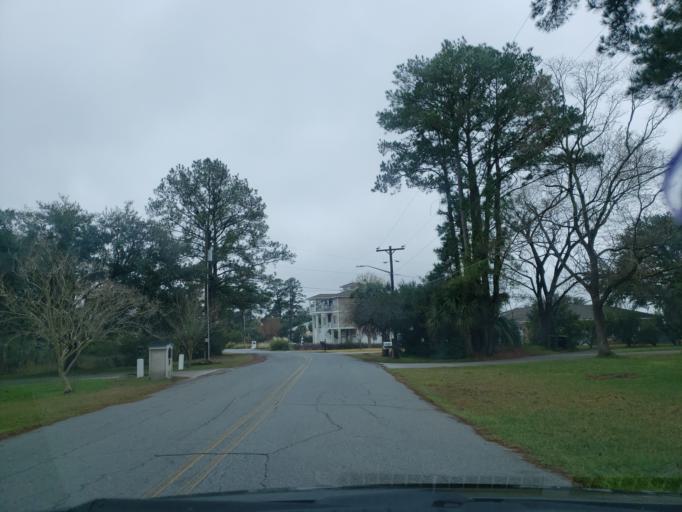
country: US
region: Georgia
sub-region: Chatham County
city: Georgetown
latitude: 31.9792
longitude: -81.1830
